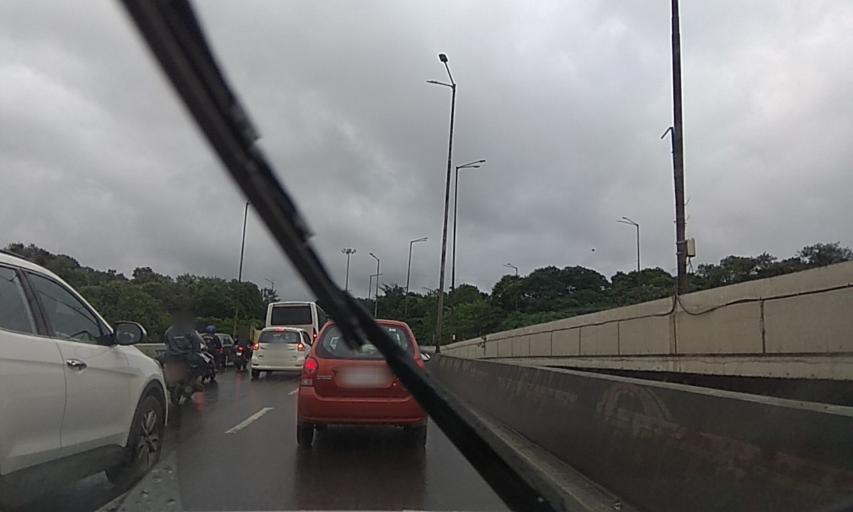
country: IN
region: Maharashtra
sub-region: Pune Division
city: Khadki
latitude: 18.5541
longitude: 73.8630
